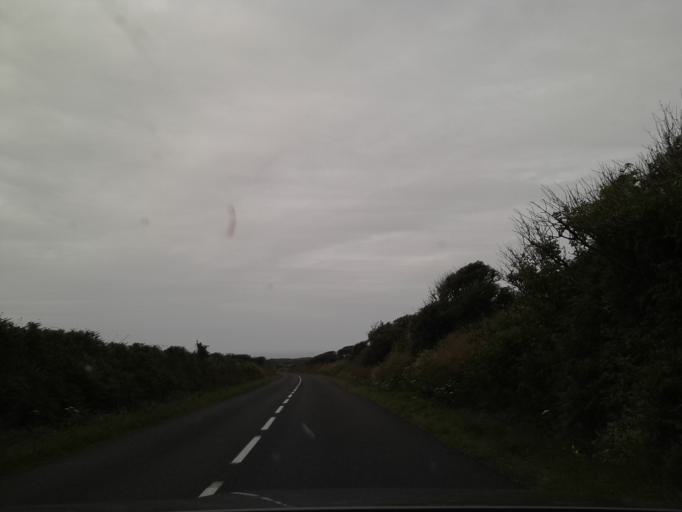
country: FR
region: Lower Normandy
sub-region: Departement de la Manche
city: Beaumont-Hague
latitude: 49.6997
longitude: -1.9265
